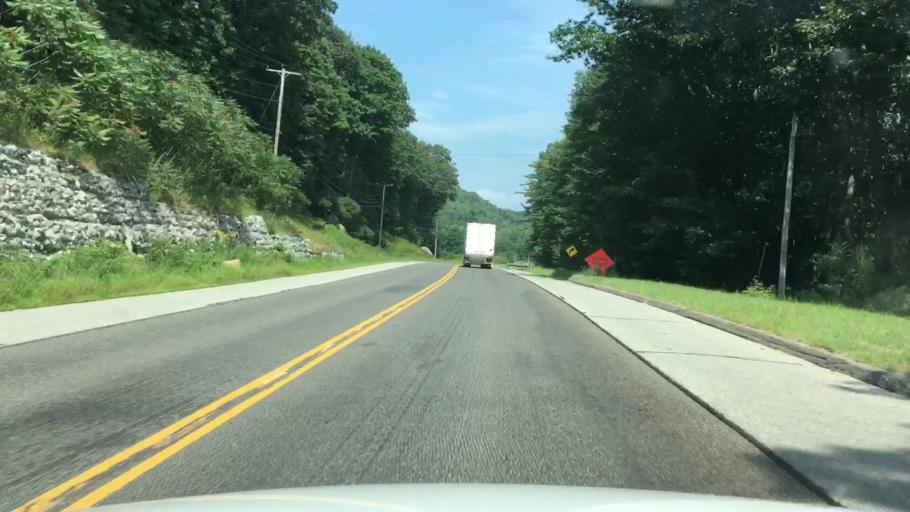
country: US
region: Maine
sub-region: Androscoggin County
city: Turner
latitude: 44.3084
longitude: -70.2659
